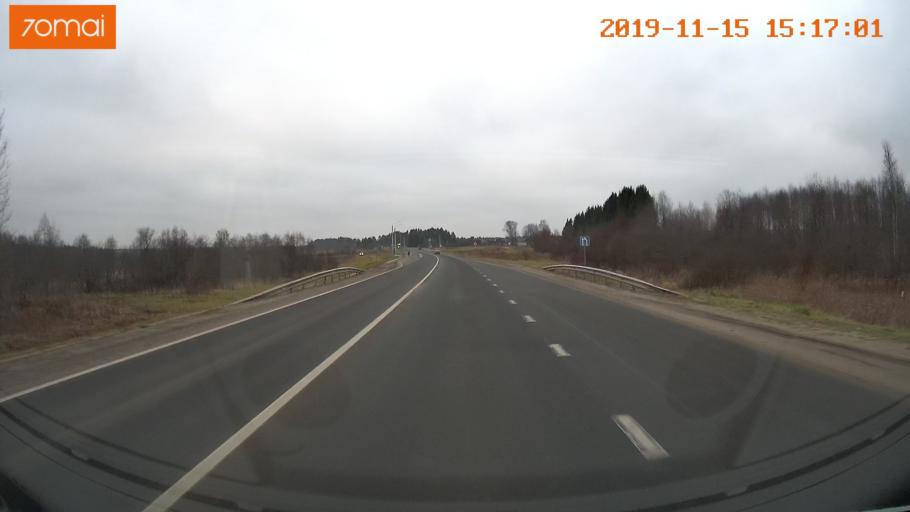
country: RU
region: Jaroslavl
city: Danilov
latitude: 58.2670
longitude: 40.1852
